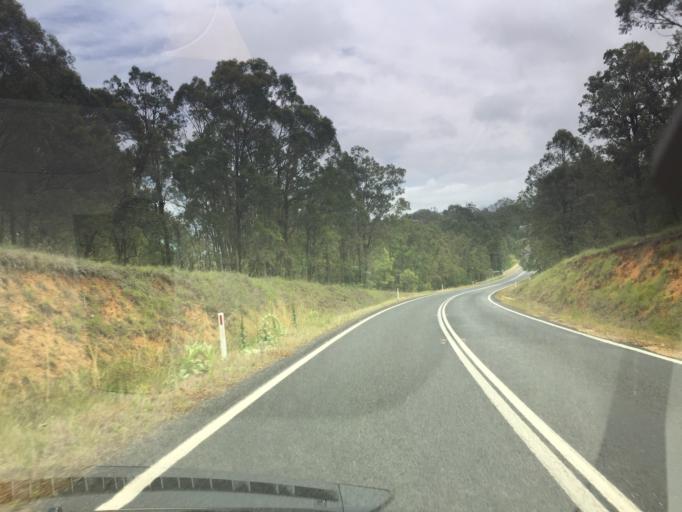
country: AU
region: New South Wales
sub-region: Bega Valley
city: Bega
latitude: -36.6378
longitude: 149.5778
